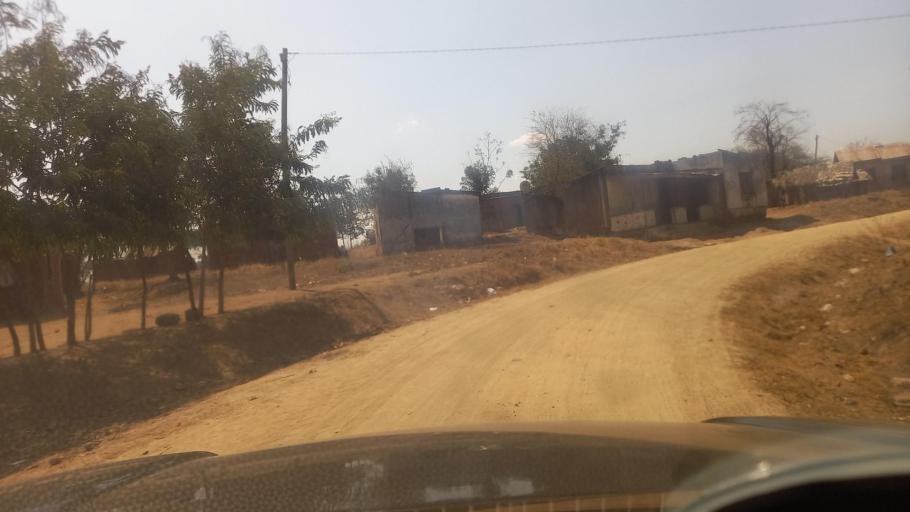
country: TZ
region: Morogoro
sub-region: Kilosa
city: Magole
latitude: -6.3217
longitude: 37.3736
